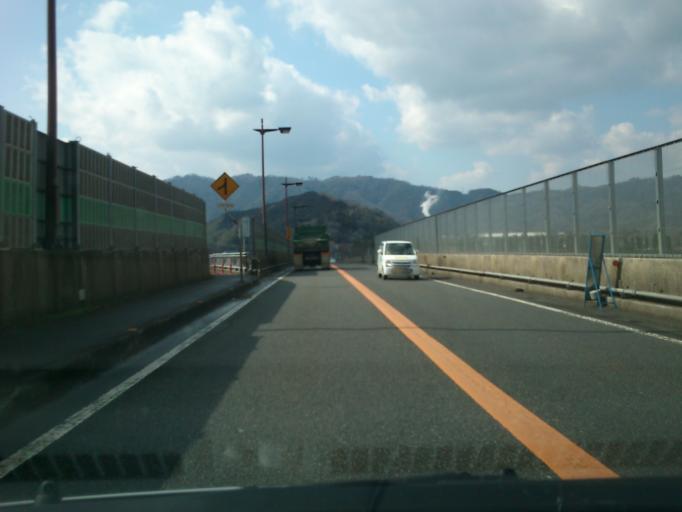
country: JP
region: Kyoto
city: Miyazu
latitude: 35.5518
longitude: 135.1599
